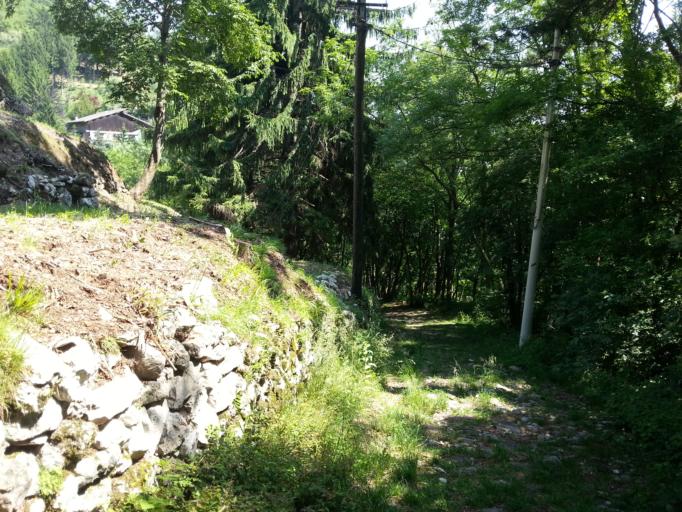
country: IT
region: Lombardy
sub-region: Provincia di Varese
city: Viggiu
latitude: 45.8768
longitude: 8.9024
